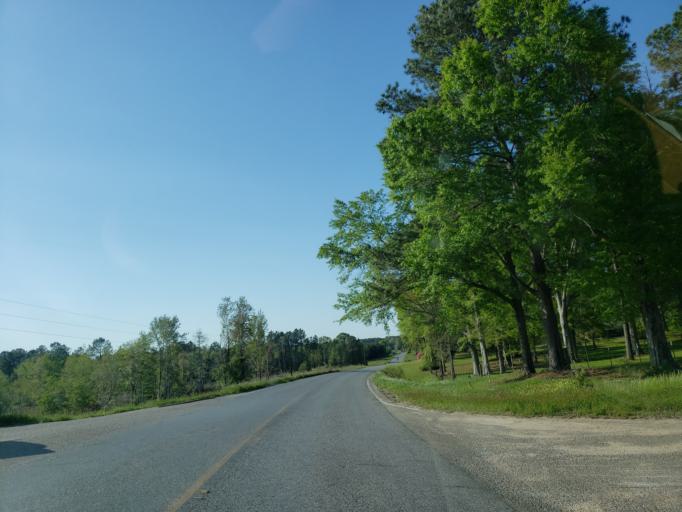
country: US
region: Mississippi
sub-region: Perry County
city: Richton
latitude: 31.4825
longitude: -89.0164
